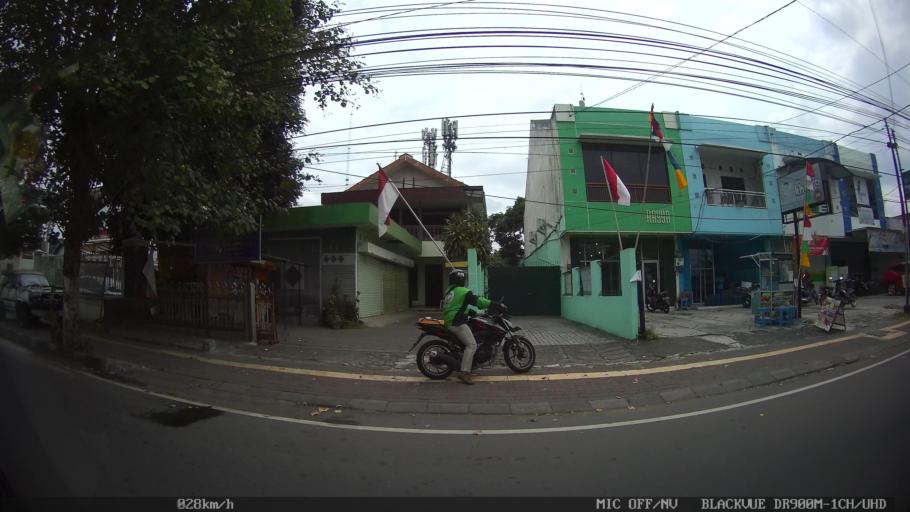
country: ID
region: Daerah Istimewa Yogyakarta
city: Yogyakarta
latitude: -7.7896
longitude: 110.3935
